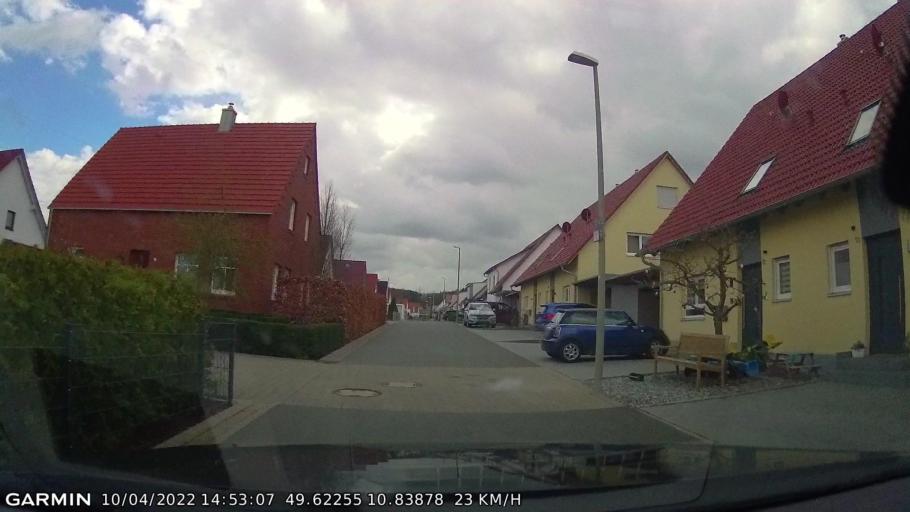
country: DE
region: Bavaria
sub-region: Regierungsbezirk Mittelfranken
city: Weisendorf
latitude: 49.6225
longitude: 10.8388
